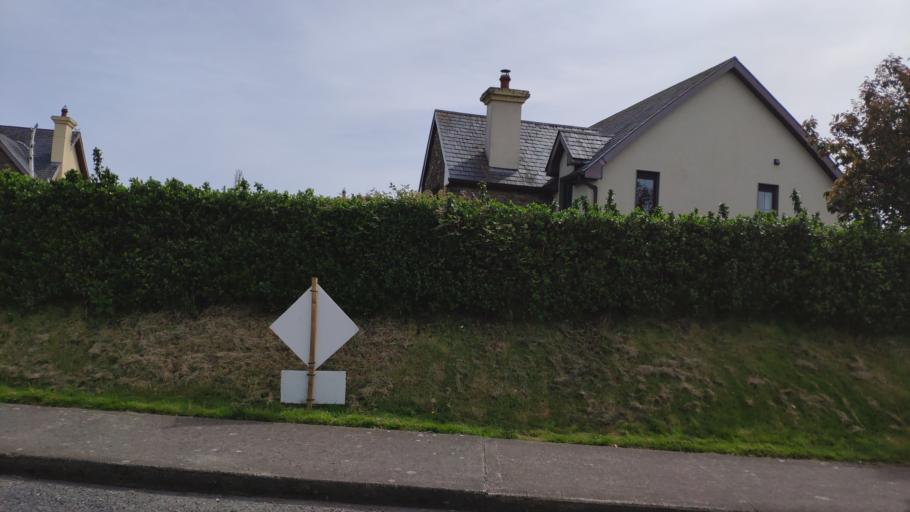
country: IE
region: Munster
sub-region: County Cork
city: Blarney
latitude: 51.9785
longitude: -8.5135
